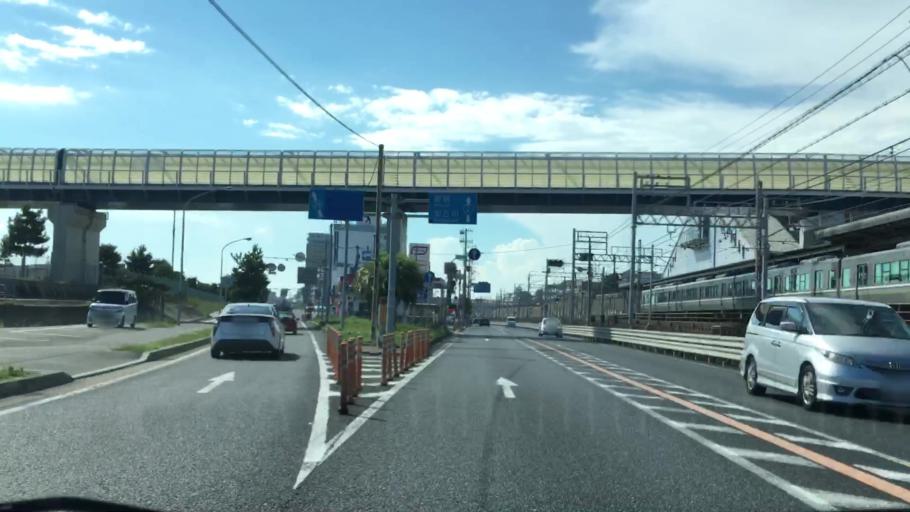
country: JP
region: Hyogo
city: Akashi
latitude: 34.6436
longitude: 135.0181
